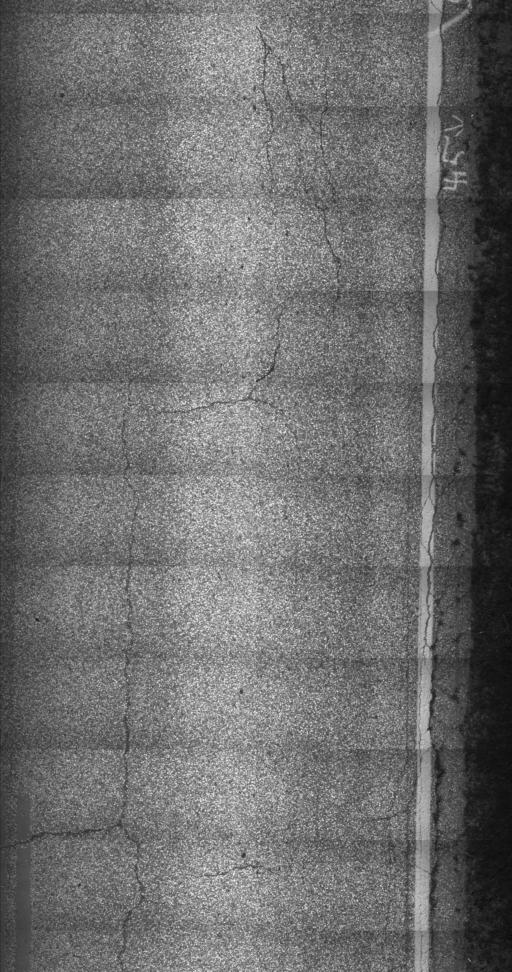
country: US
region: Vermont
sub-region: Rutland County
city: West Rutland
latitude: 43.5805
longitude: -73.0402
